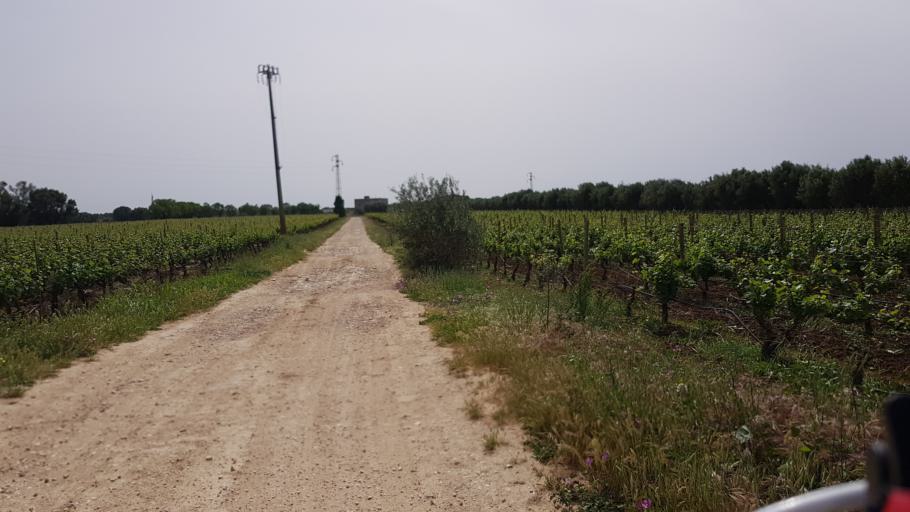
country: IT
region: Apulia
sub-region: Provincia di Brindisi
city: Mesagne
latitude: 40.6323
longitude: 17.8138
